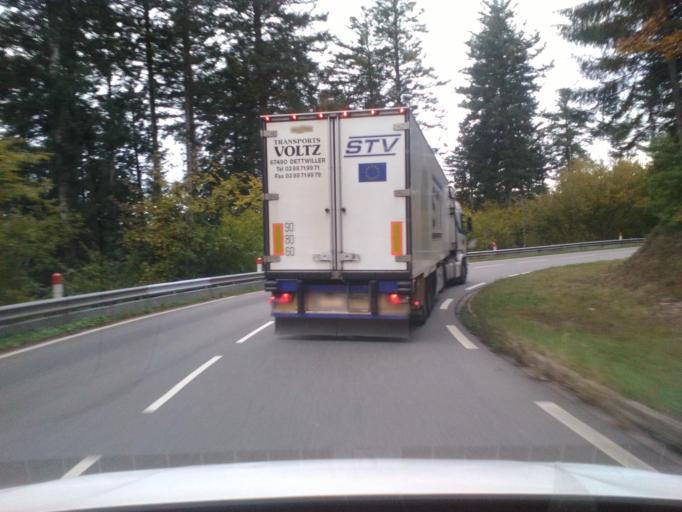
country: FR
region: Lorraine
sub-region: Departement des Vosges
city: Ban-de-Laveline
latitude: 48.3307
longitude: 7.0934
